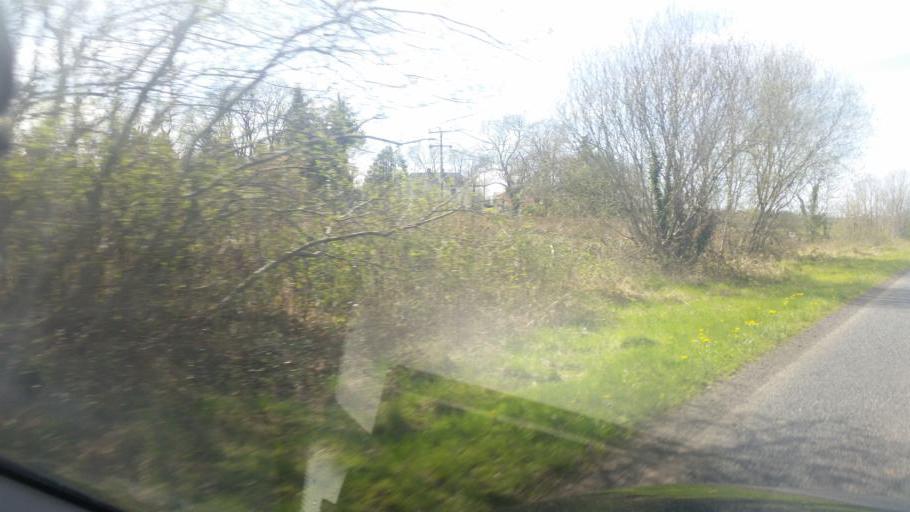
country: IE
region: Ulster
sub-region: County Donegal
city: Ballyshannon
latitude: 54.4672
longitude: -8.0427
